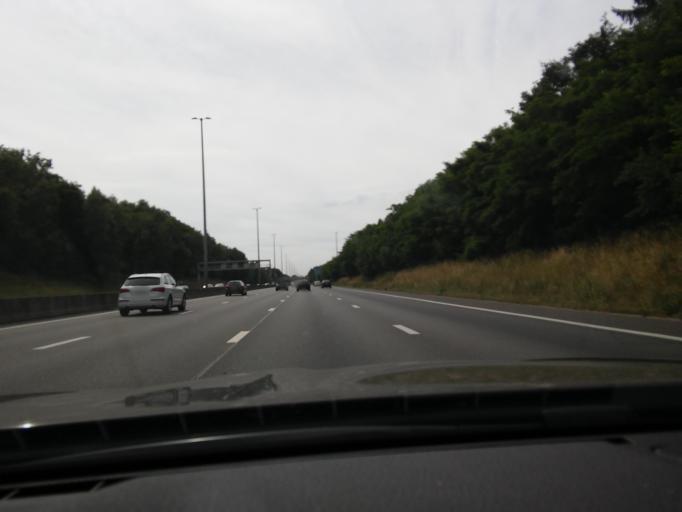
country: BE
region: Flanders
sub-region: Provincie Vlaams-Brabant
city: Kortenberg
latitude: 50.8696
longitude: 4.5309
